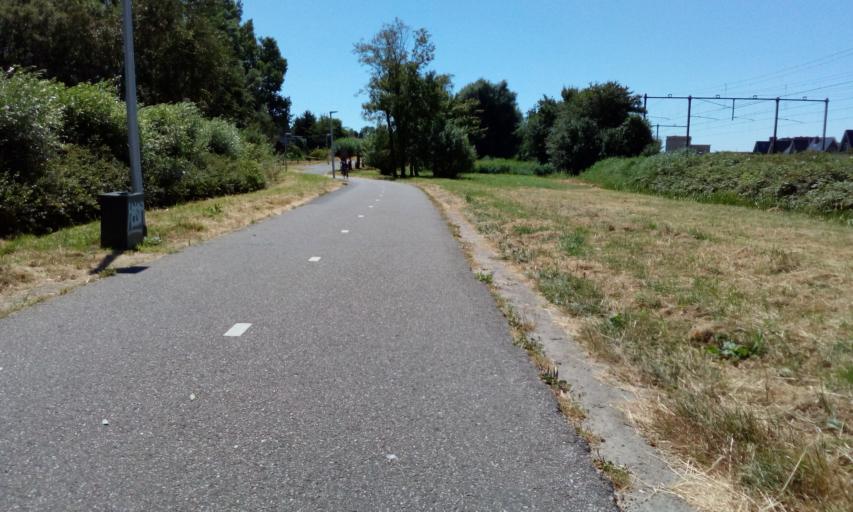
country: NL
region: South Holland
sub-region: Gemeente Leiden
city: Leiden
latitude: 52.1846
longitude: 4.4985
